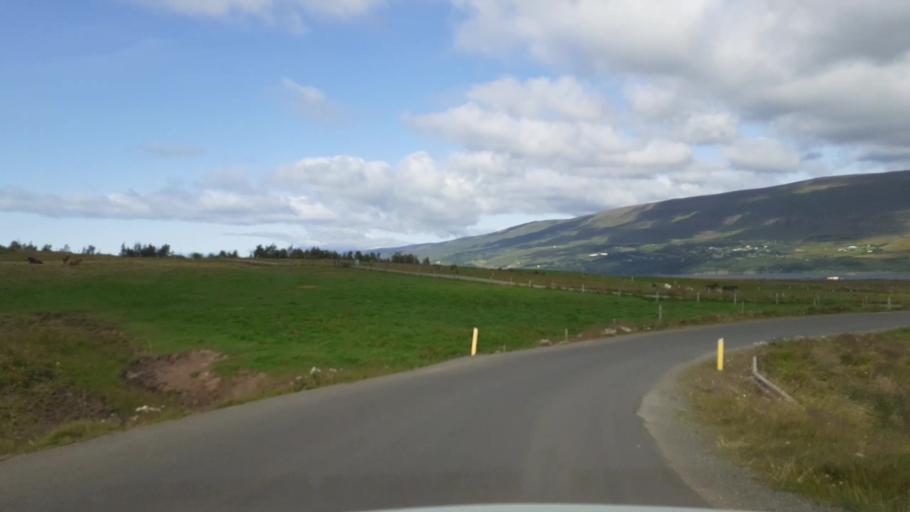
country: IS
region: Northeast
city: Akureyri
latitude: 65.6505
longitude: -18.0979
